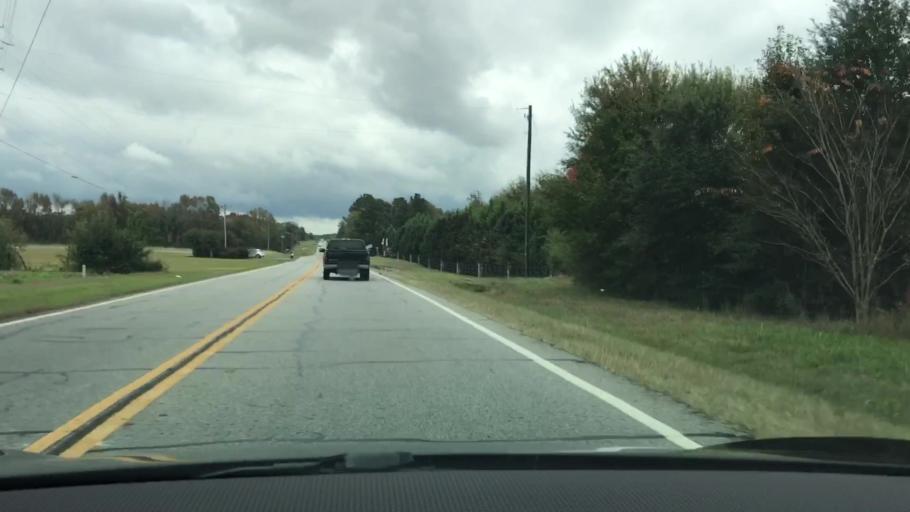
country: US
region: Georgia
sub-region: Oconee County
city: Watkinsville
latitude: 33.8359
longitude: -83.3824
